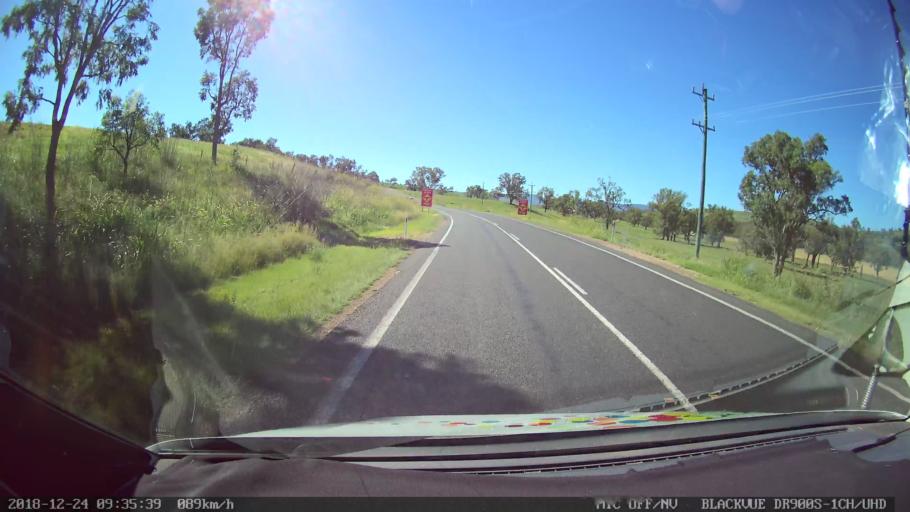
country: AU
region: New South Wales
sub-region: Liverpool Plains
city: Quirindi
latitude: -31.6320
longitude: 150.7187
